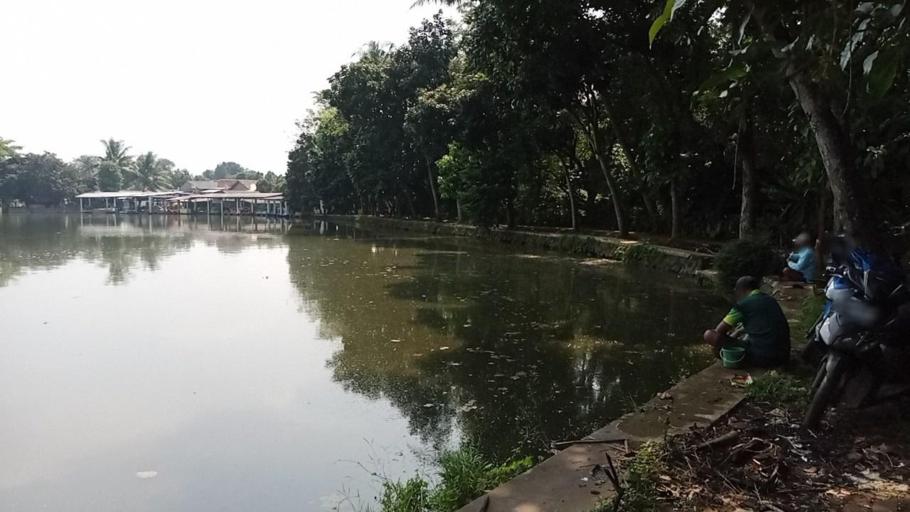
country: ID
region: West Java
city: Parung
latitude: -6.4218
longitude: 106.7494
